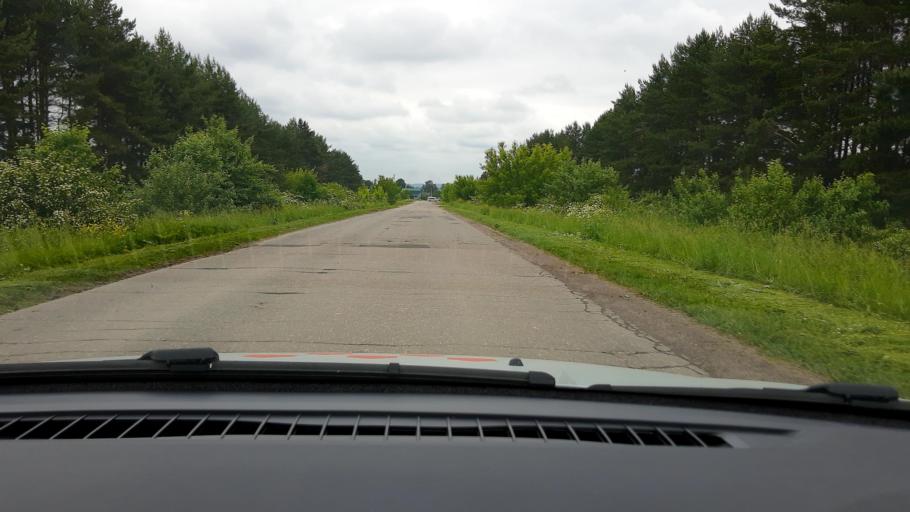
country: RU
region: Nizjnij Novgorod
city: Bogorodsk
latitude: 56.0848
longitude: 43.5124
